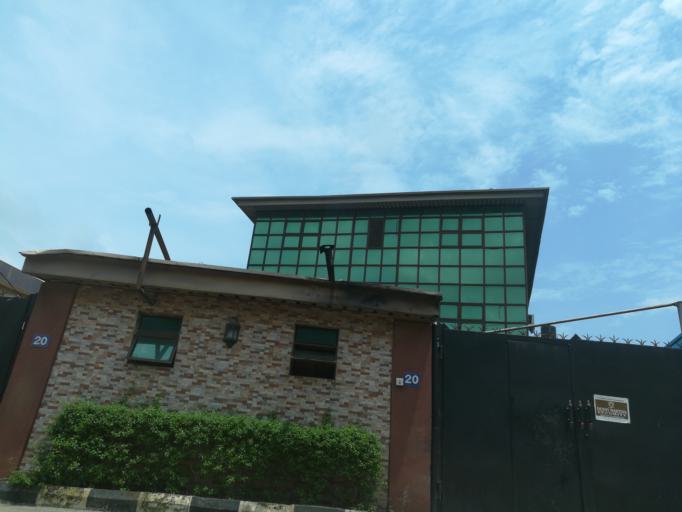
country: NG
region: Lagos
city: Oshodi
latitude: 6.5489
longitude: 3.3264
